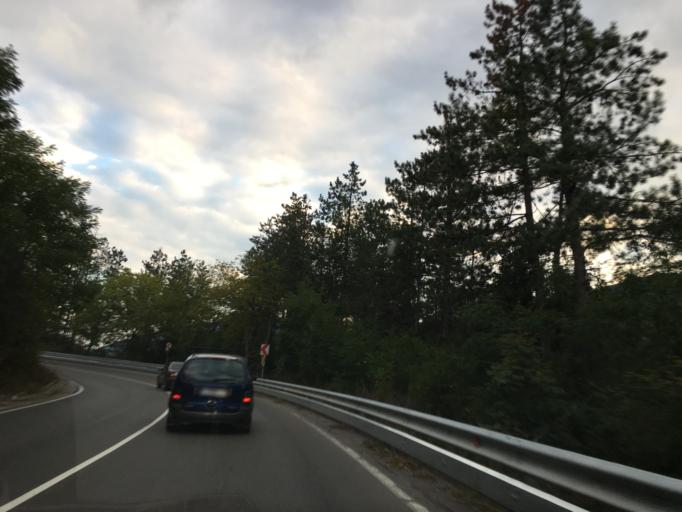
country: BG
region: Sofiya
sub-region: Obshtina Svoge
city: Svoge
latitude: 42.9385
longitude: 23.3819
